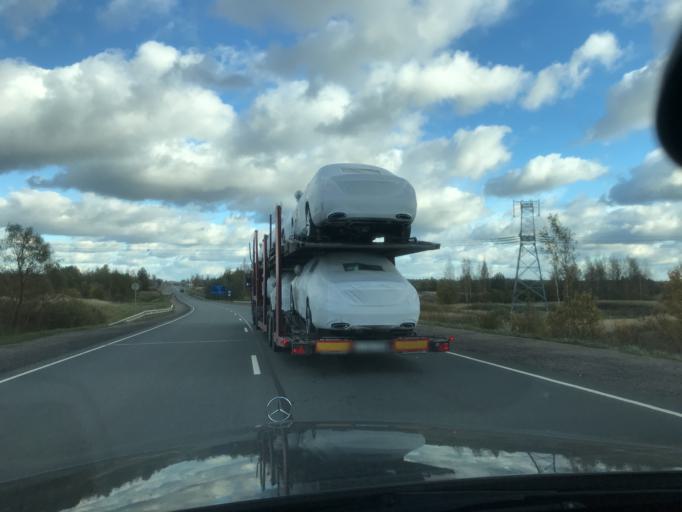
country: RU
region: Pskov
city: Novosokol'niki
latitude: 56.3221
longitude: 30.1211
